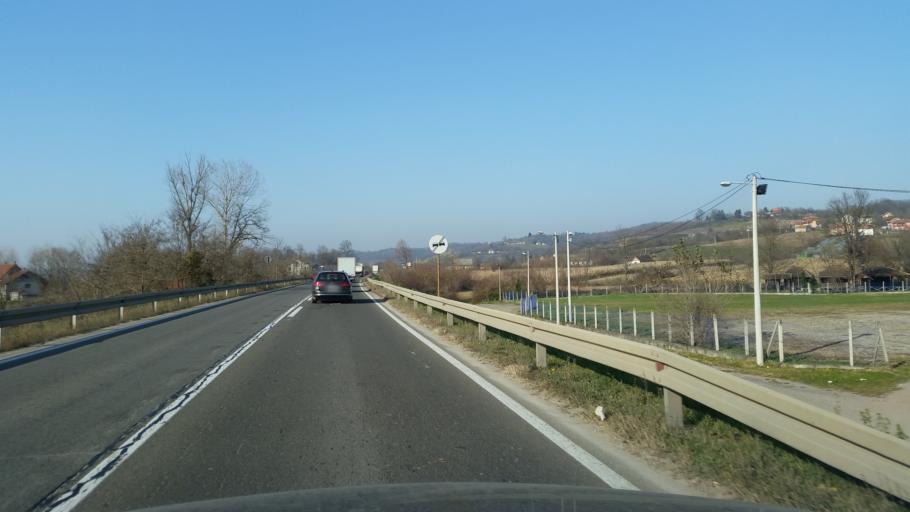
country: RS
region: Central Serbia
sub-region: Belgrade
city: Lazarevac
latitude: 44.3226
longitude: 20.2251
